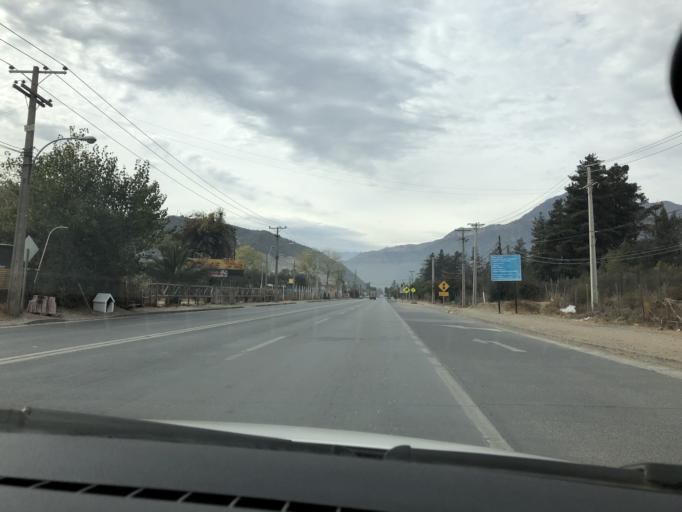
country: CL
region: Santiago Metropolitan
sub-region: Provincia de Cordillera
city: Puente Alto
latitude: -33.5981
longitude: -70.5169
